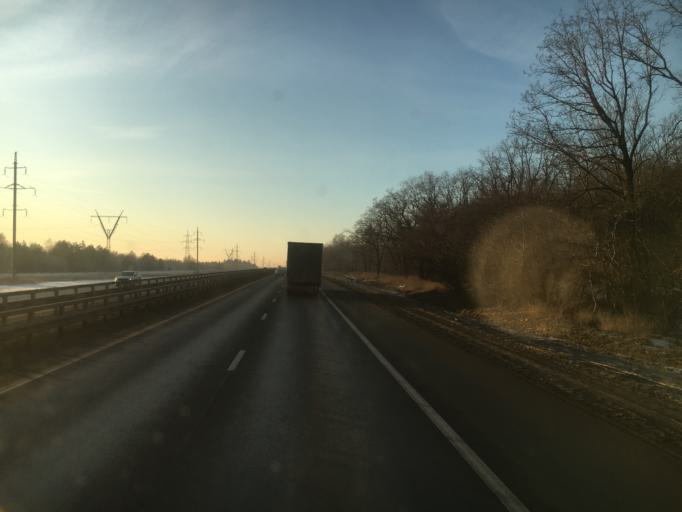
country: RU
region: Samara
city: Pribrezhnyy
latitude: 53.5184
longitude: 49.8089
